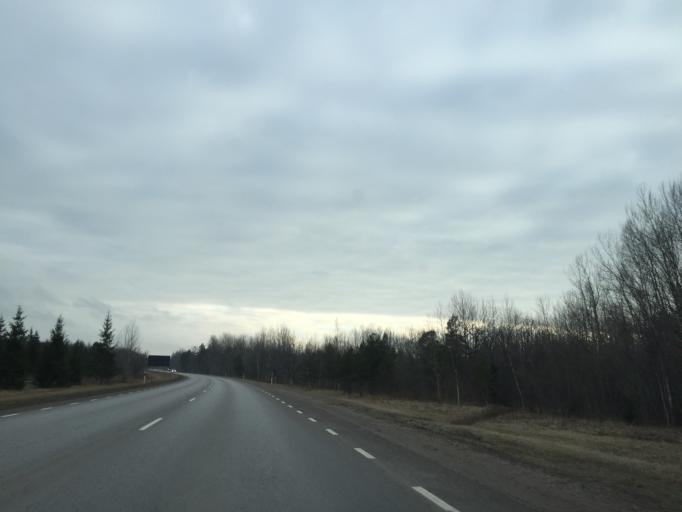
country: EE
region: Saare
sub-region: Orissaare vald
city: Orissaare
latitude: 58.4702
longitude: 22.8165
